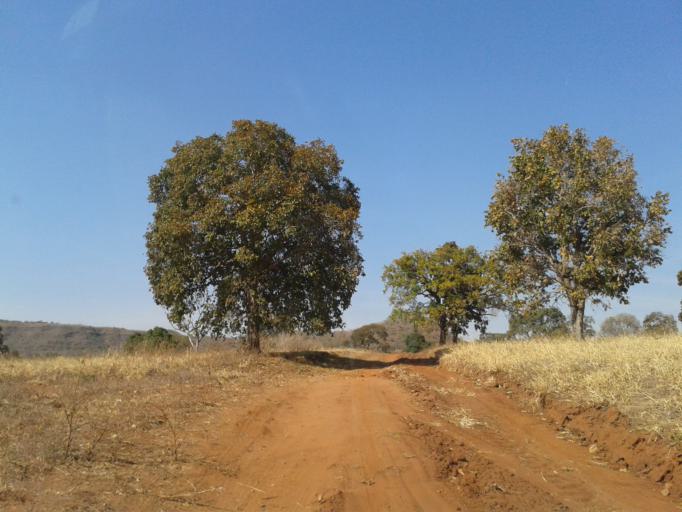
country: BR
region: Minas Gerais
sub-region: Santa Vitoria
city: Santa Vitoria
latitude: -19.2177
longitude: -50.0425
